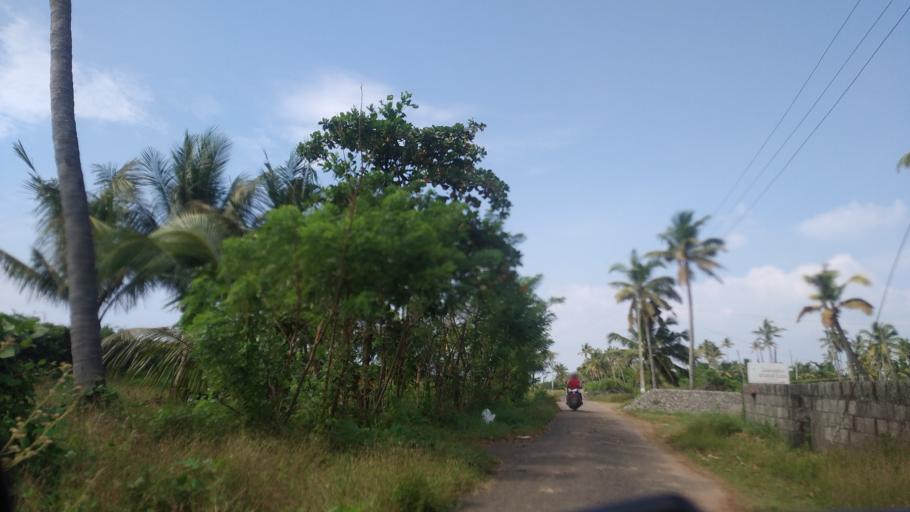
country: IN
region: Kerala
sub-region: Ernakulam
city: Elur
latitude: 10.0705
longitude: 76.1976
